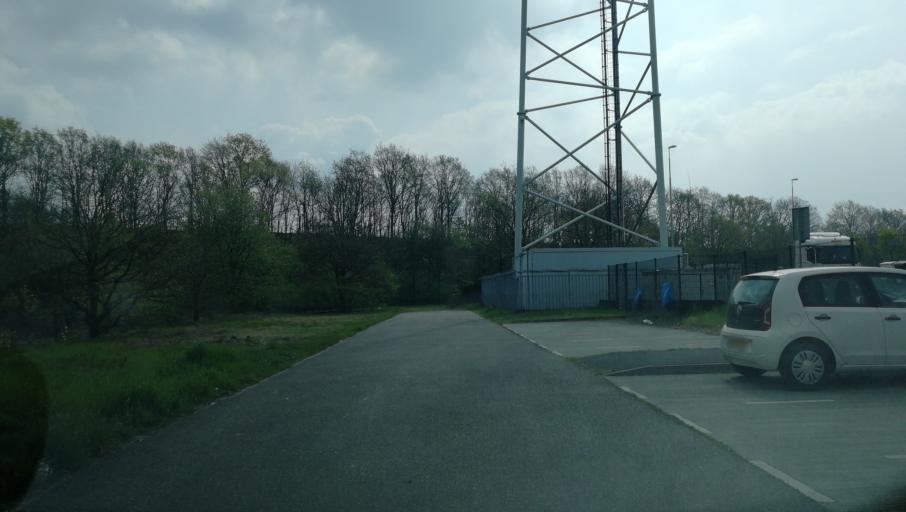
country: NL
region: Limburg
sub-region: Gemeente Venlo
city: Venlo
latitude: 51.3866
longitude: 6.2146
